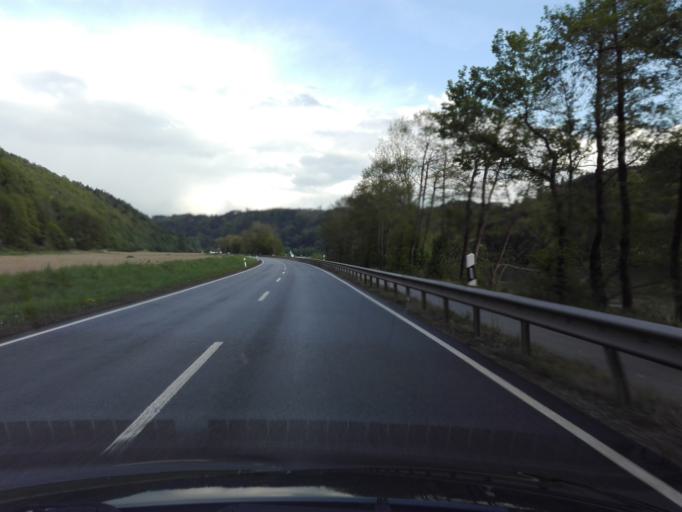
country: DE
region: Bavaria
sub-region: Lower Bavaria
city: Thyrnau
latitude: 48.5699
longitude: 13.5536
